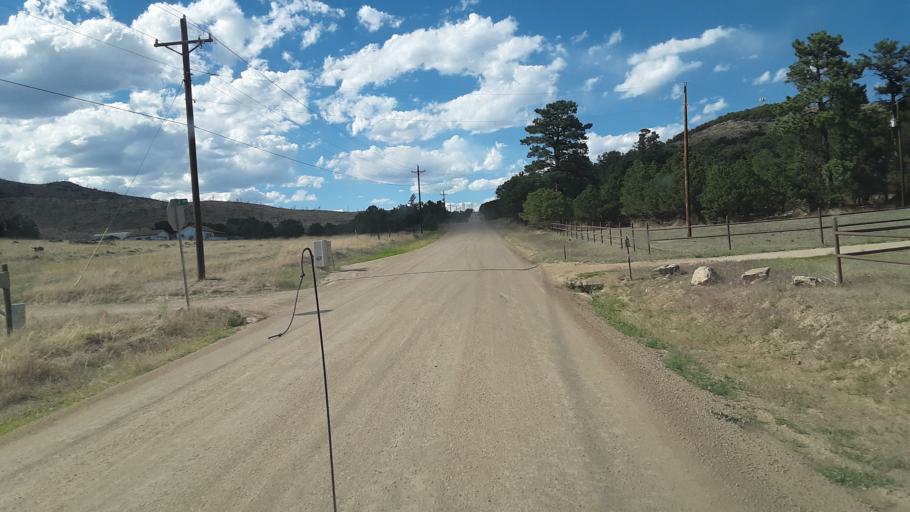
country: US
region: Colorado
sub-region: Custer County
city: Westcliffe
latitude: 38.3174
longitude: -105.4870
